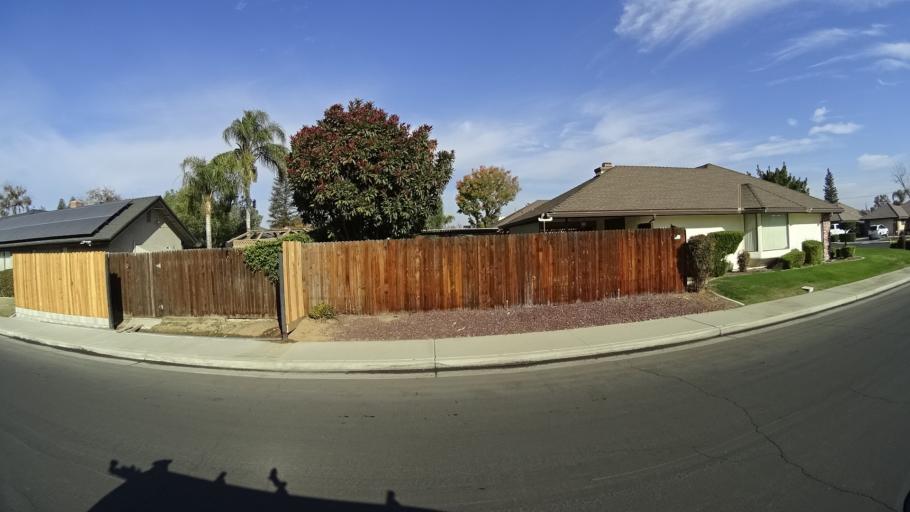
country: US
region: California
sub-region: Kern County
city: Greenacres
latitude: 35.4064
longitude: -119.0758
